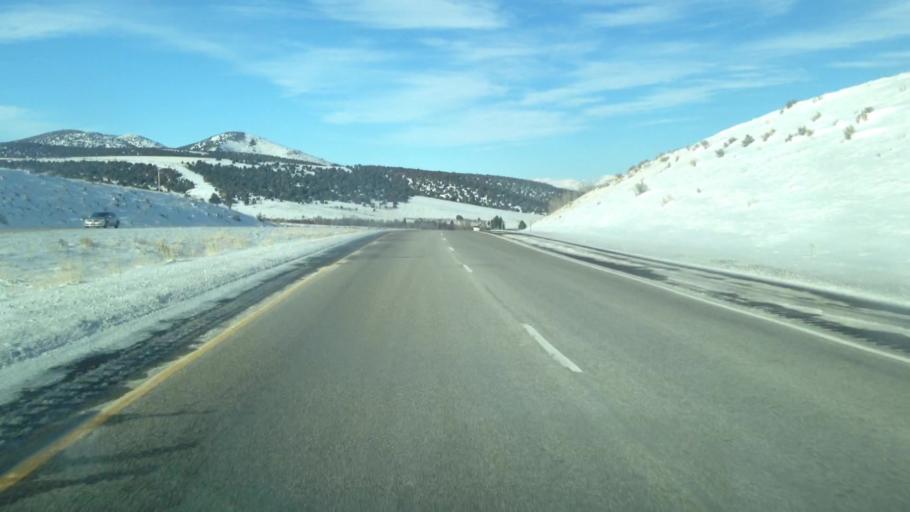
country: US
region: Idaho
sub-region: Oneida County
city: Malad City
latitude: 42.3441
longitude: -112.2266
